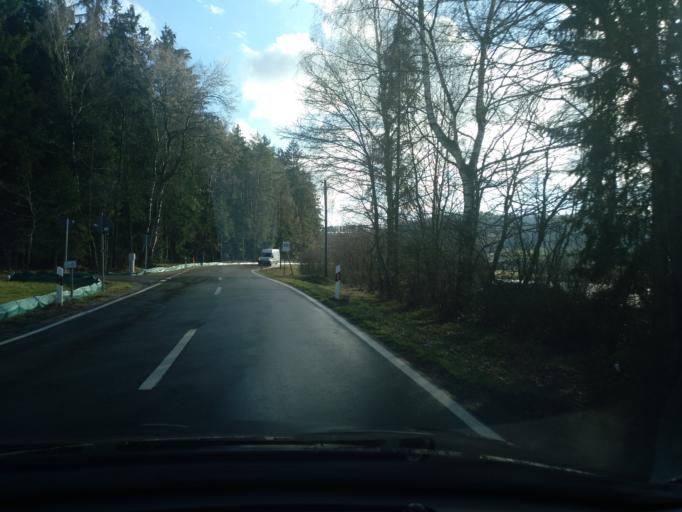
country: DE
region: Bavaria
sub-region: Upper Palatinate
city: Zandt
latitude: 49.1139
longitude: 12.7162
